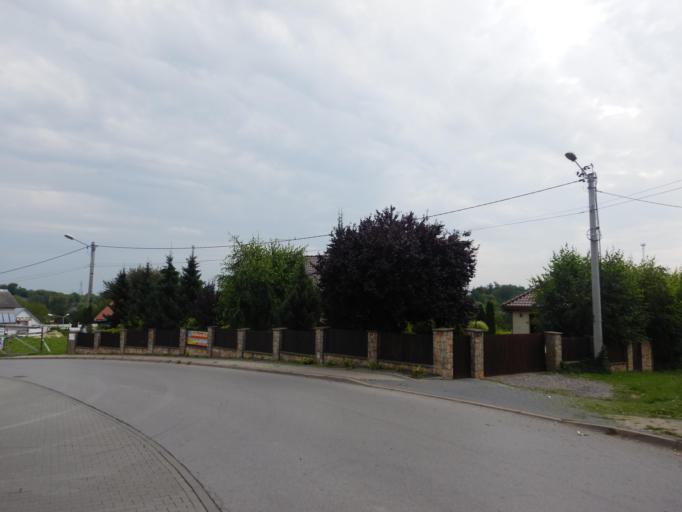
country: PL
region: Swietokrzyskie
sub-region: Powiat opatowski
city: Opatow
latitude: 50.7979
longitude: 21.4321
